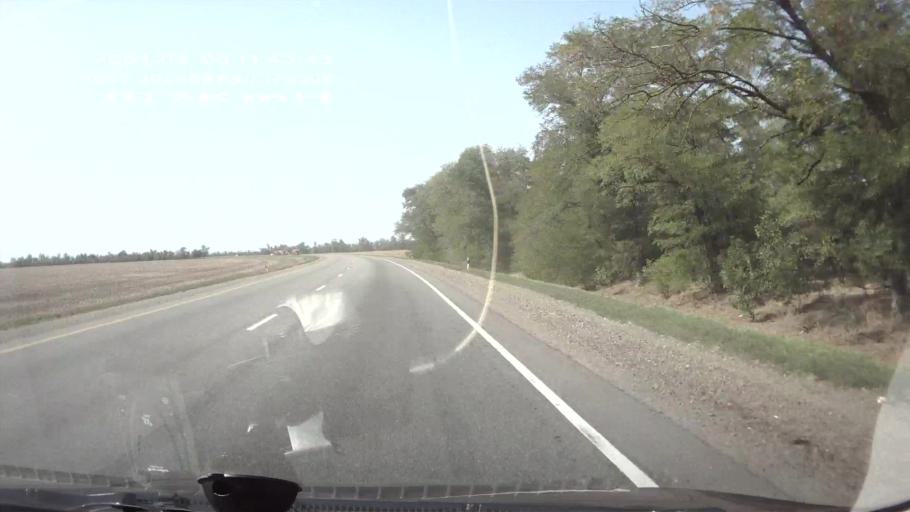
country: RU
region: Krasnodarskiy
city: Tbilisskaya
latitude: 45.4024
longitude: 40.1785
